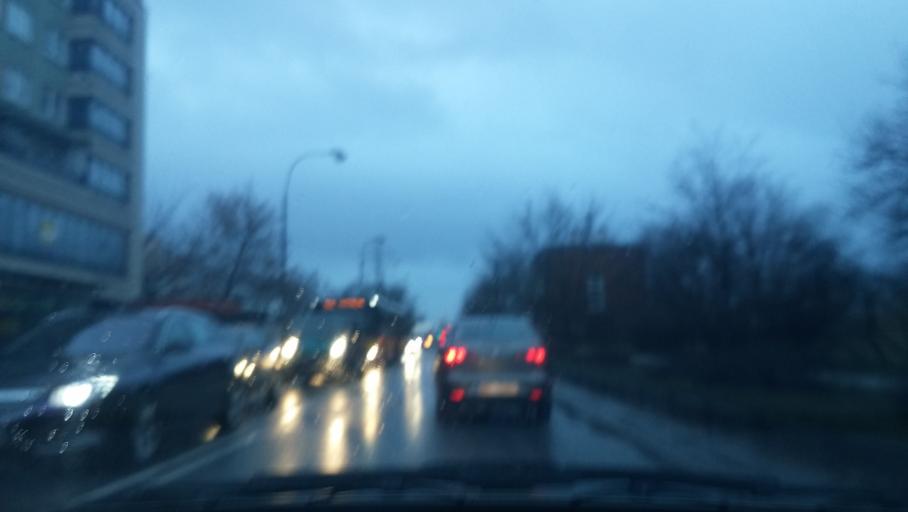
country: PL
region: Masovian Voivodeship
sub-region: Warszawa
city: Praga Poludnie
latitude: 52.2382
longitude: 21.0995
